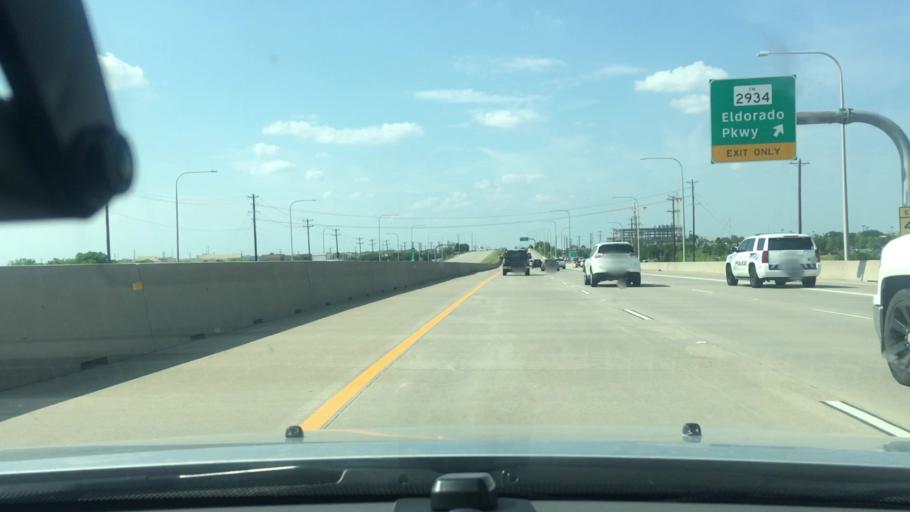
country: US
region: Texas
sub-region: Collin County
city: Frisco
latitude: 33.1686
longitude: -96.8397
